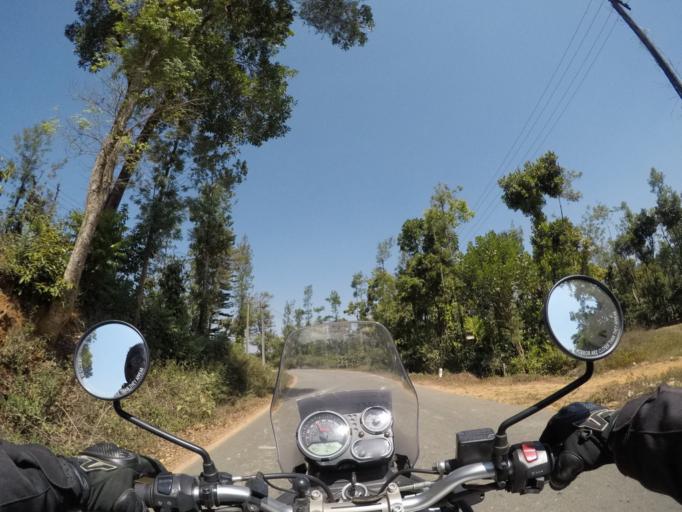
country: IN
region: Karnataka
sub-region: Chikmagalur
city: Mudigere
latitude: 13.0397
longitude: 75.6884
